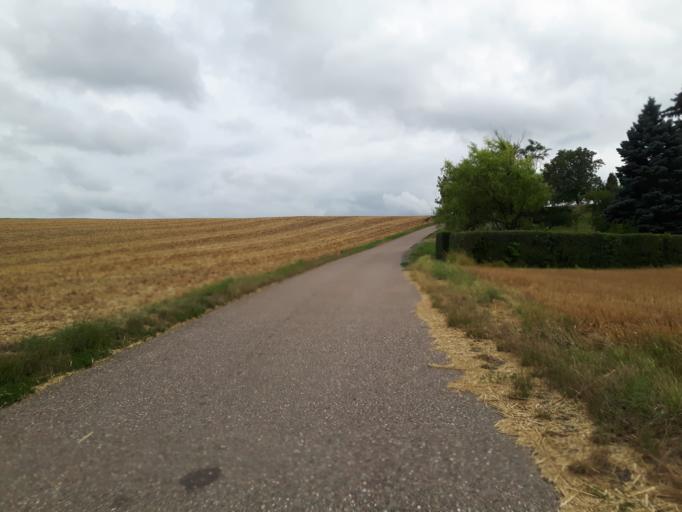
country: DE
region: Baden-Wuerttemberg
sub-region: Regierungsbezirk Stuttgart
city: Nordheim
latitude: 49.1121
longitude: 9.1088
